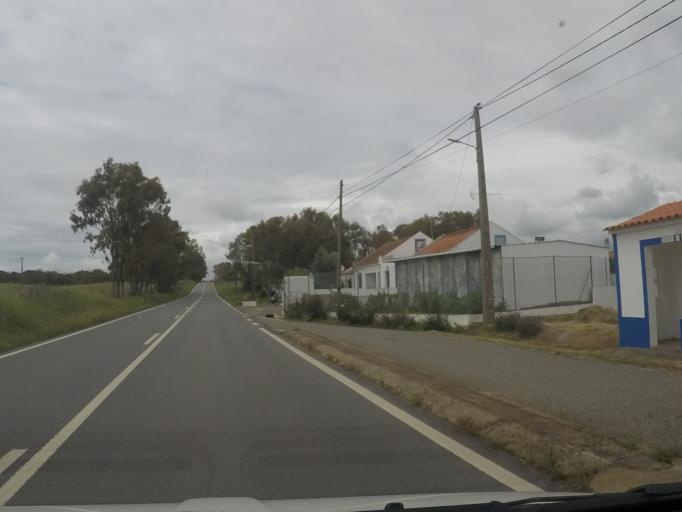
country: PT
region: Setubal
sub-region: Santiago do Cacem
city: Cercal
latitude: 37.8609
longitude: -8.7168
